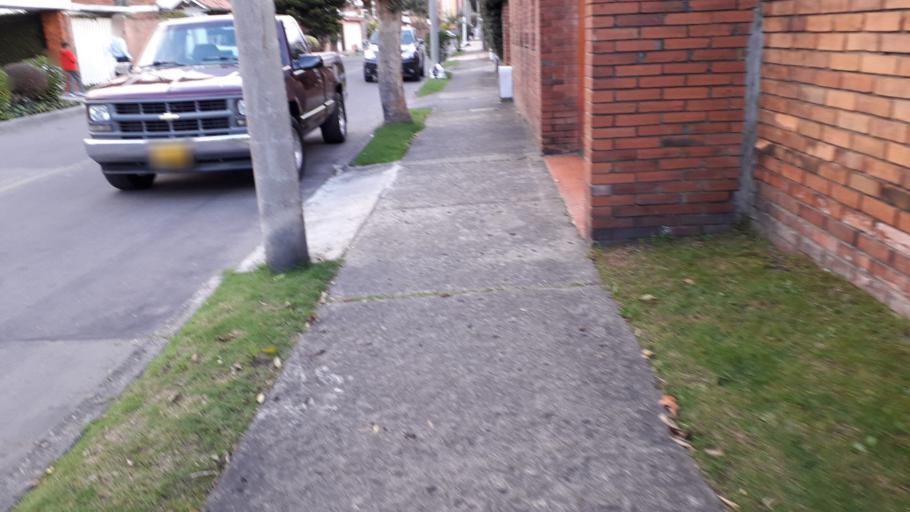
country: CO
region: Bogota D.C.
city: Bogota
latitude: 4.6486
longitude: -74.0908
